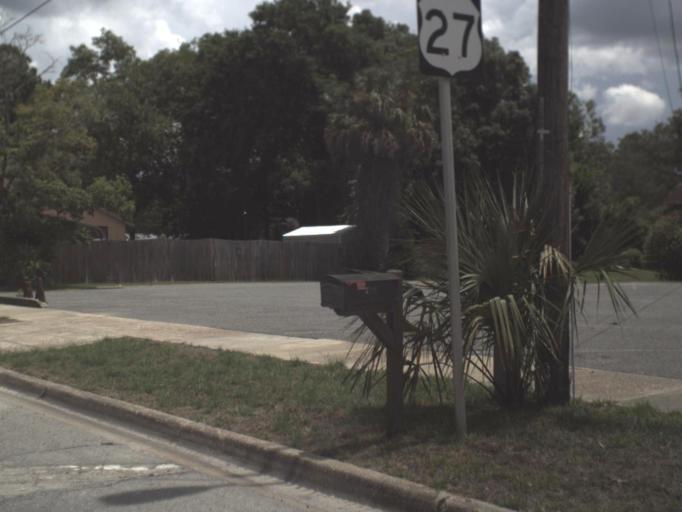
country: US
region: Florida
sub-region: Taylor County
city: Perry
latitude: 30.1116
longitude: -83.5887
